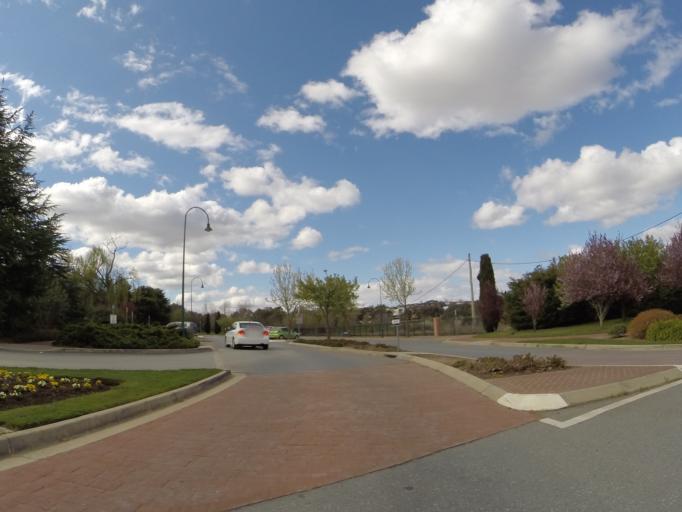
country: AU
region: Australian Capital Territory
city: Belconnen
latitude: -35.1927
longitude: 149.0872
